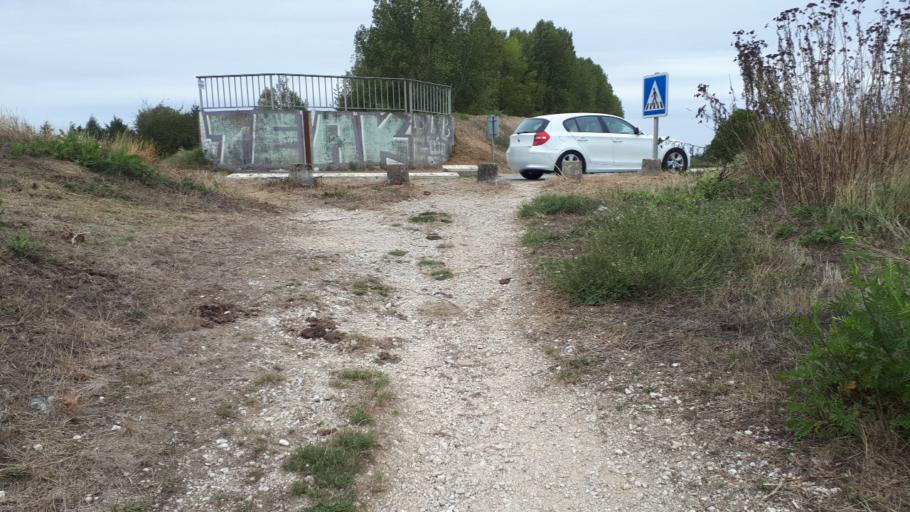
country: FR
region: Centre
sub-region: Departement du Loir-et-Cher
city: Saint-Gervais-la-Foret
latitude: 47.5695
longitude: 1.3406
